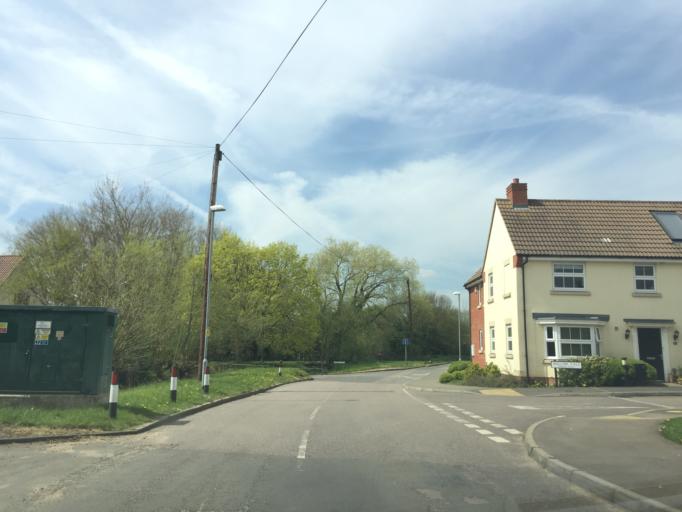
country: GB
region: England
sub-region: Essex
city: Saffron Walden
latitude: 51.9866
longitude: 0.2101
